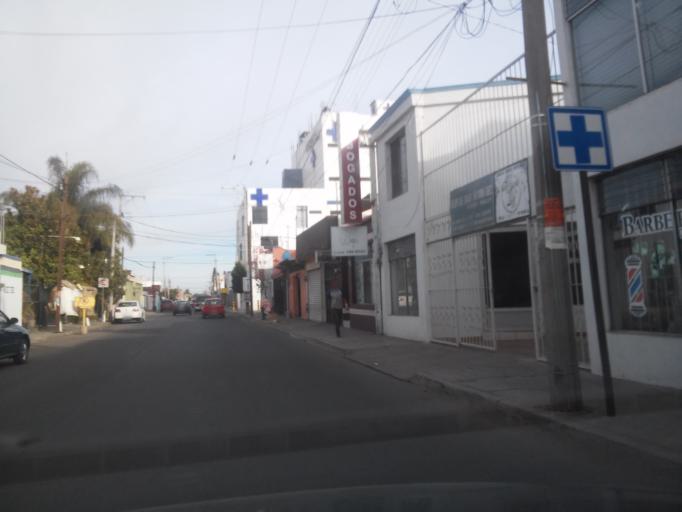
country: MX
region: Durango
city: Victoria de Durango
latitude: 24.0250
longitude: -104.6521
